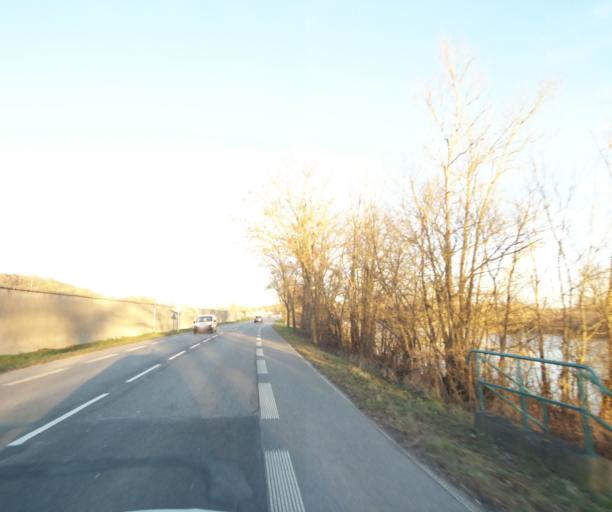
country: FR
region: Lorraine
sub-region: Departement de Meurthe-et-Moselle
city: Laneuveville-devant-Nancy
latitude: 48.6618
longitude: 6.2444
